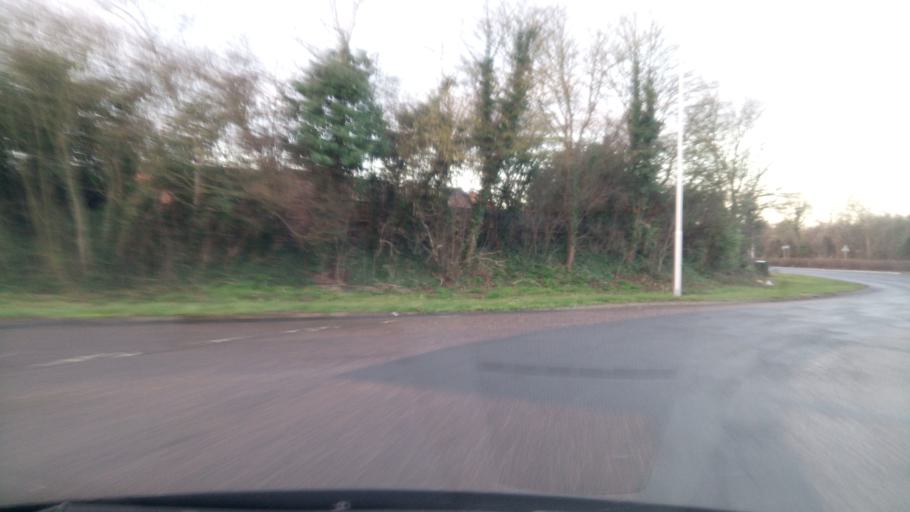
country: GB
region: England
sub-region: Peterborough
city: Marholm
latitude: 52.5766
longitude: -0.2925
